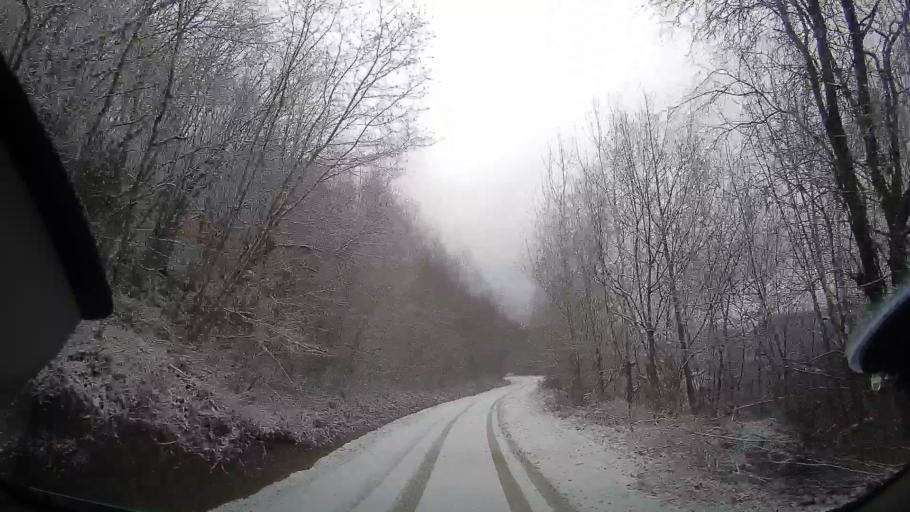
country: RO
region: Cluj
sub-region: Comuna Maguri-Racatau
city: Maguri-Racatau
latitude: 46.6562
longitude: 23.1919
